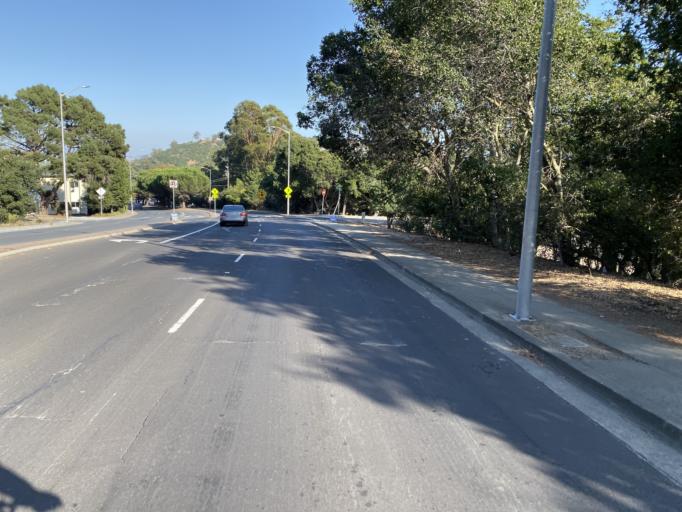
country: US
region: California
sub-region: San Mateo County
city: Belmont
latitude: 37.5112
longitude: -122.2980
